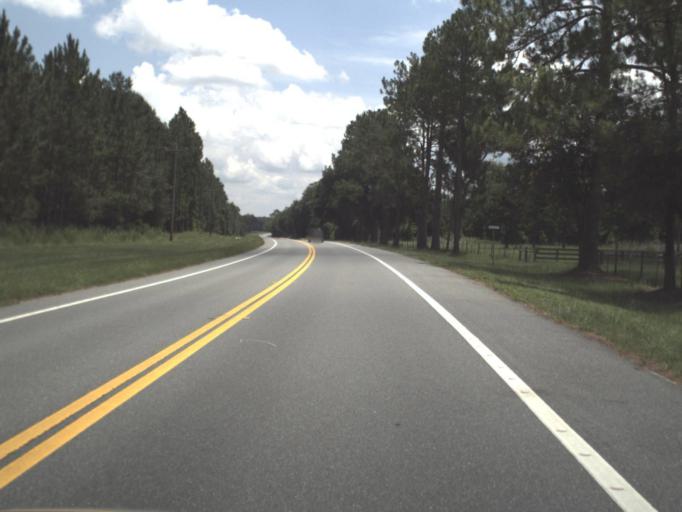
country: US
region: Florida
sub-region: Union County
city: Lake Butler
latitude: 30.0082
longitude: -82.4631
